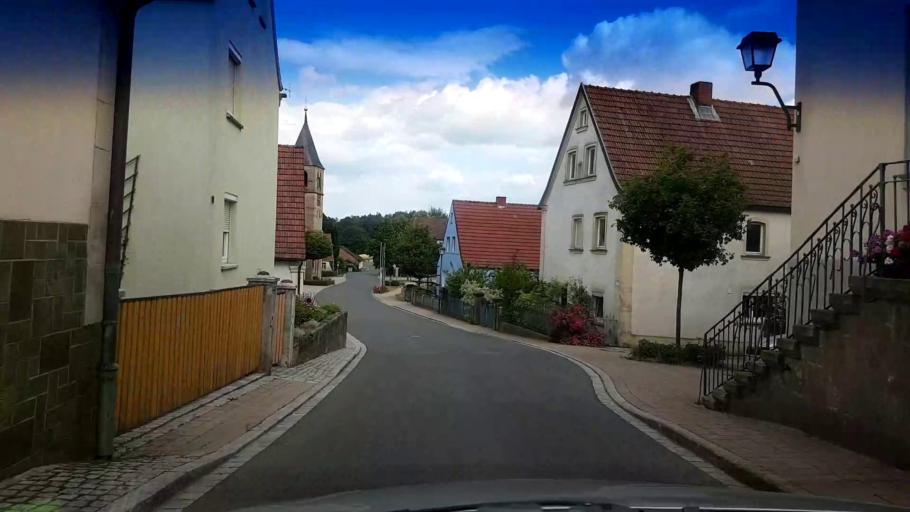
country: DE
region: Bavaria
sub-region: Upper Franconia
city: Gerach
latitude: 50.0031
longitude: 10.7920
